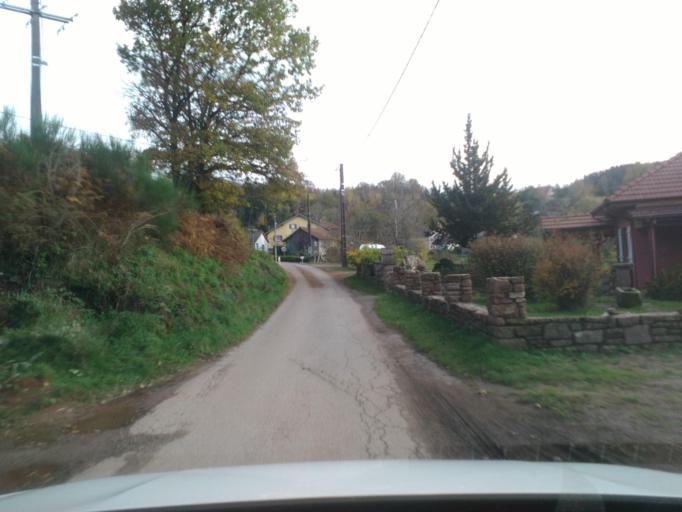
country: FR
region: Lorraine
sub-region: Departement des Vosges
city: Senones
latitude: 48.4109
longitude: 7.0544
